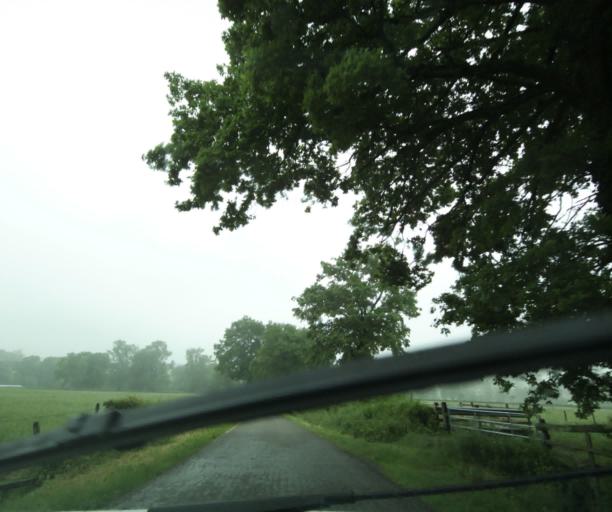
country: FR
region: Bourgogne
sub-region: Departement de Saone-et-Loire
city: Charolles
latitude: 46.4068
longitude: 4.2867
